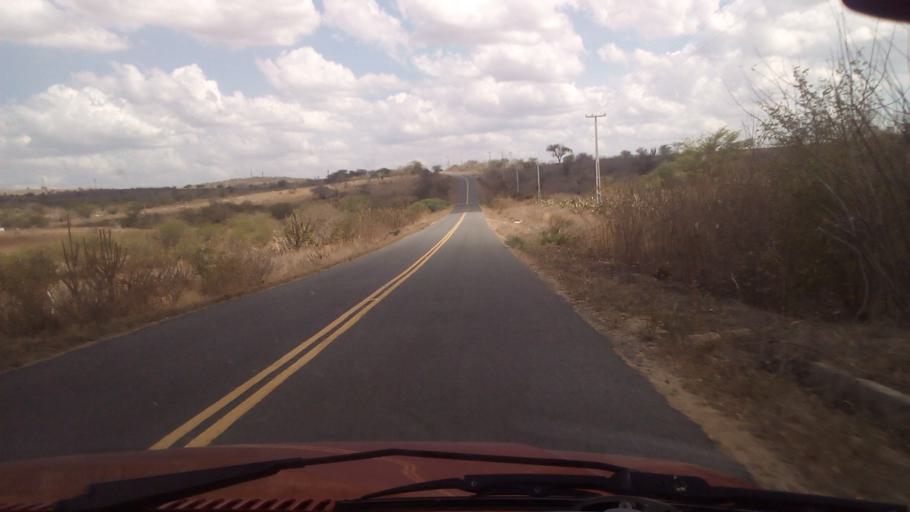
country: BR
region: Paraiba
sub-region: Cacimba De Dentro
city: Cacimba de Dentro
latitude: -6.6943
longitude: -35.7394
